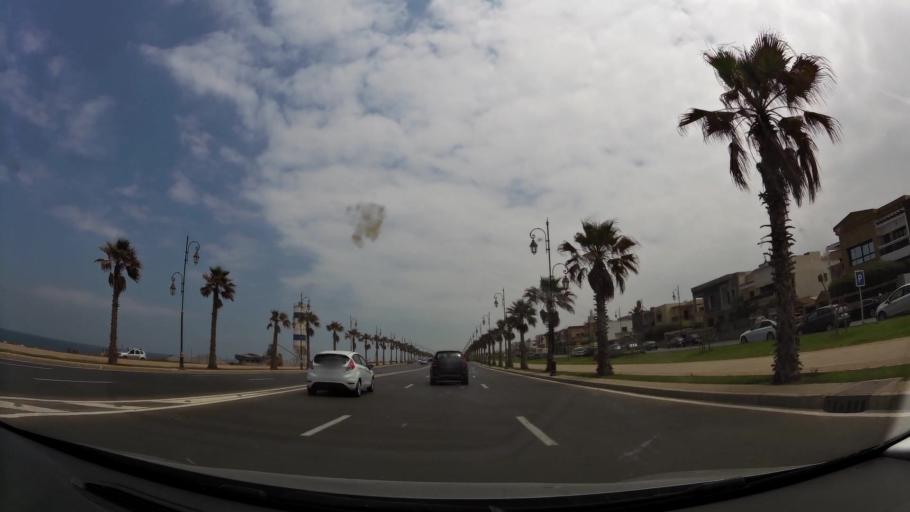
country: MA
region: Rabat-Sale-Zemmour-Zaer
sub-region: Skhirate-Temara
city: Temara
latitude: 33.9850
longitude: -6.8910
